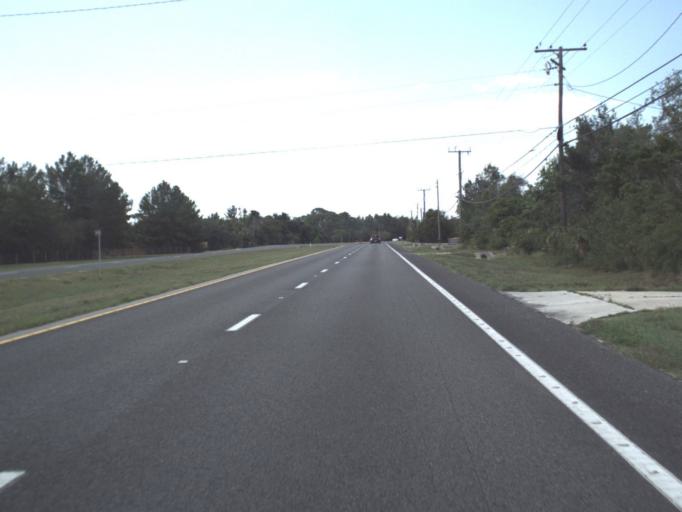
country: US
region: Florida
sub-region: Brevard County
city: Mims
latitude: 28.7337
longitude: -80.8669
